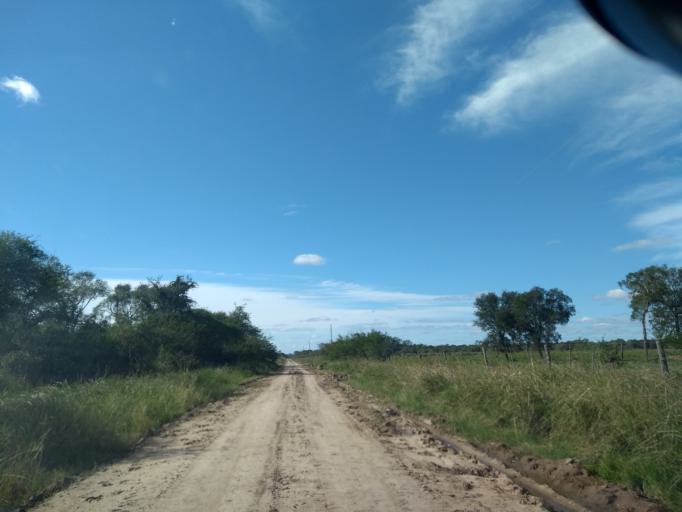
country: AR
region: Chaco
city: Colonia Benitez
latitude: -27.2905
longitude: -58.9352
